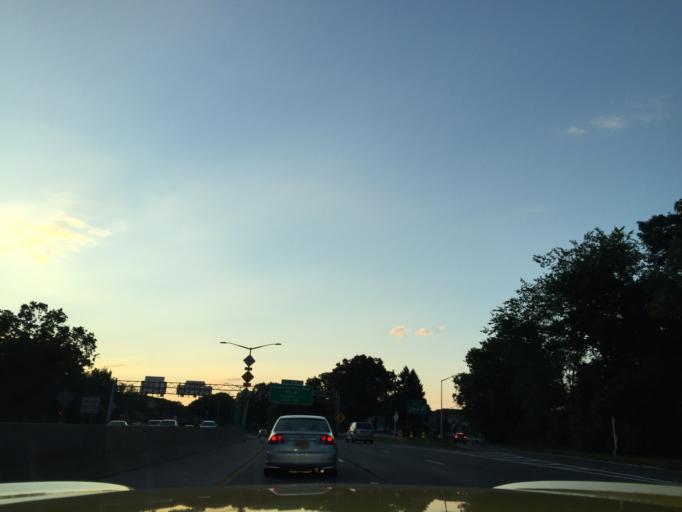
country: US
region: New York
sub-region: Nassau County
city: Bellerose
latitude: 40.7387
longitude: -73.7242
